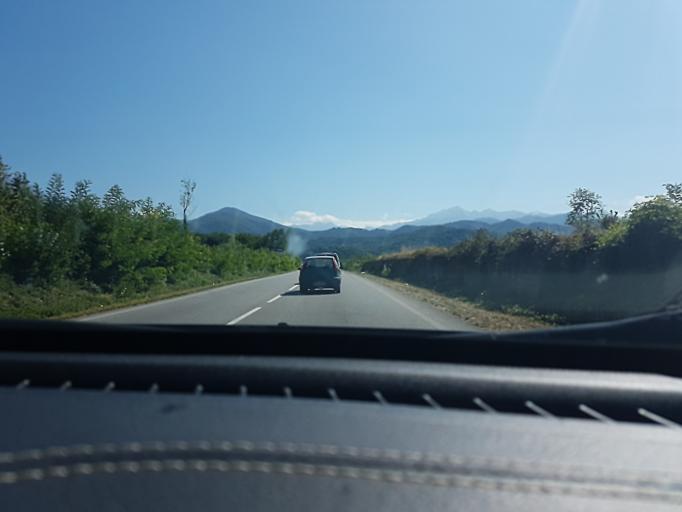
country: IT
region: Piedmont
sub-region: Provincia di Cuneo
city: Boves
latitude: 44.3509
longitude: 7.5466
